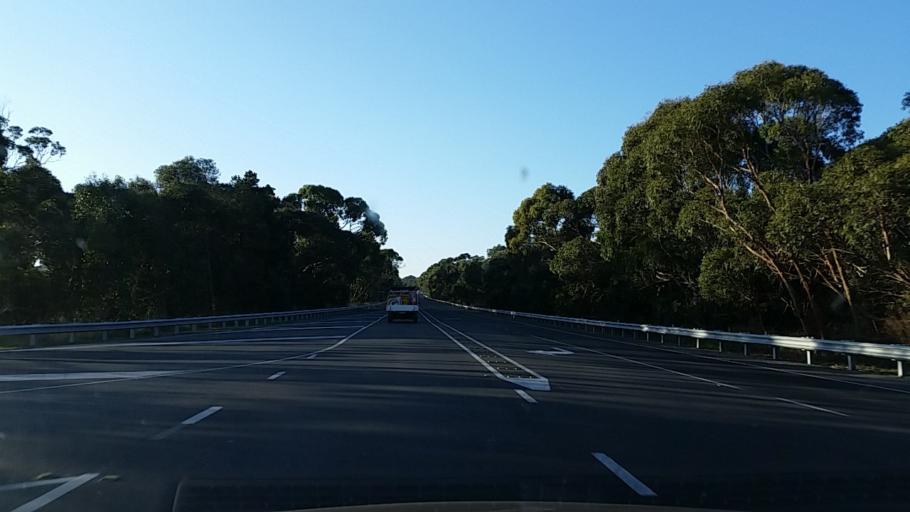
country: AU
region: South Australia
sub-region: Alexandrina
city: Mount Compass
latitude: -35.3104
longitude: 138.5820
